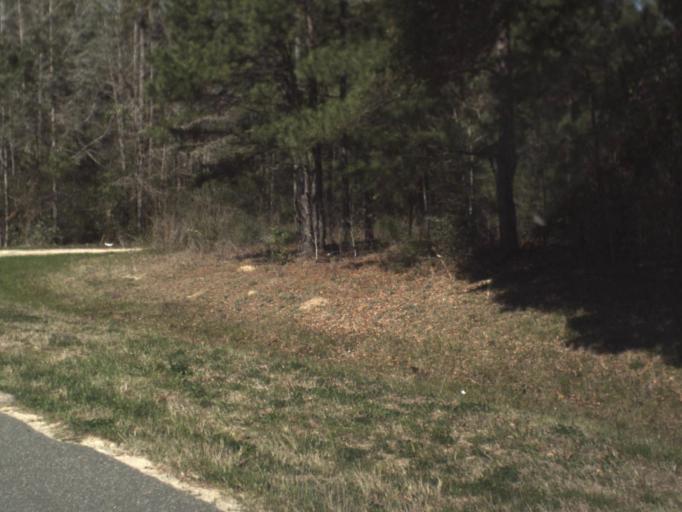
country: US
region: Florida
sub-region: Jackson County
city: Marianna
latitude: 30.7846
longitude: -85.3035
